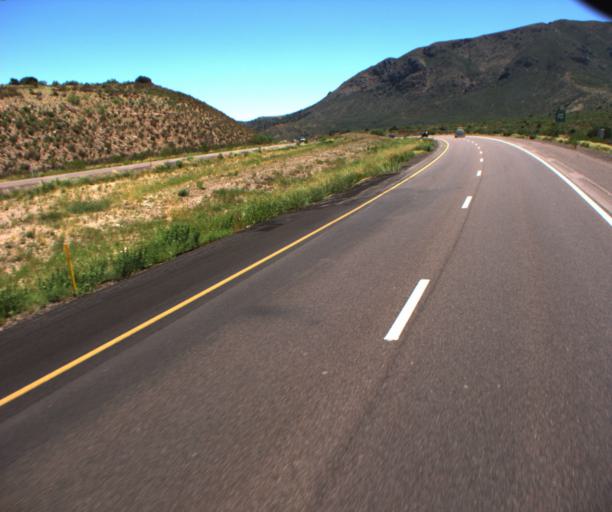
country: US
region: Arizona
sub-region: Gila County
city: Payson
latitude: 34.0446
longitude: -111.3706
